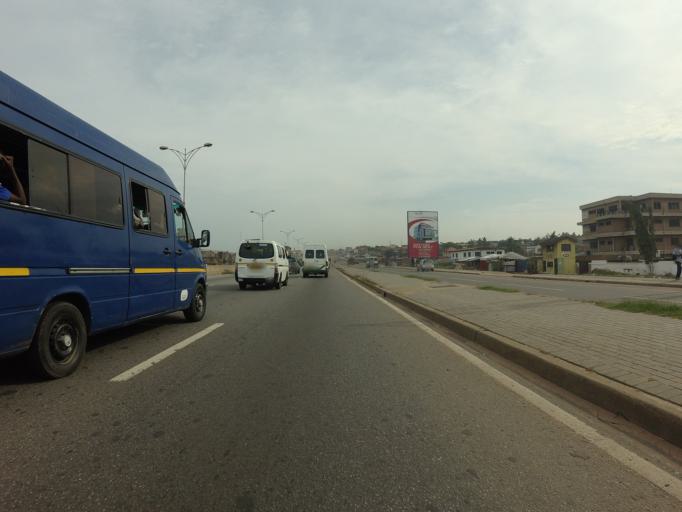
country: GH
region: Greater Accra
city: Gbawe
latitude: 5.5941
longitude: -0.2666
